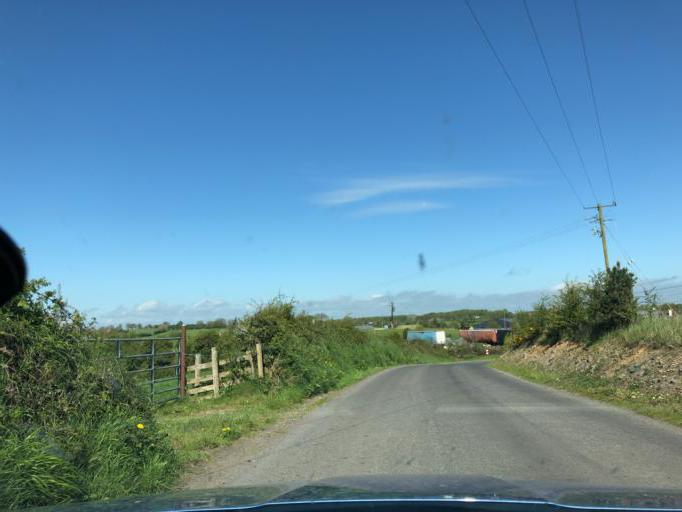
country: IE
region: Connaught
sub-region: County Galway
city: Portumna
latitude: 53.1560
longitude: -8.2950
